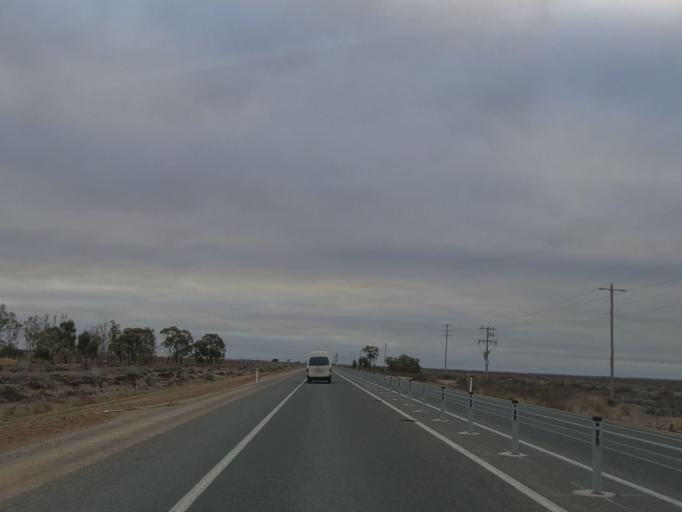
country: AU
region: Victoria
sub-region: Swan Hill
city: Swan Hill
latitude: -35.5186
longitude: 143.7299
